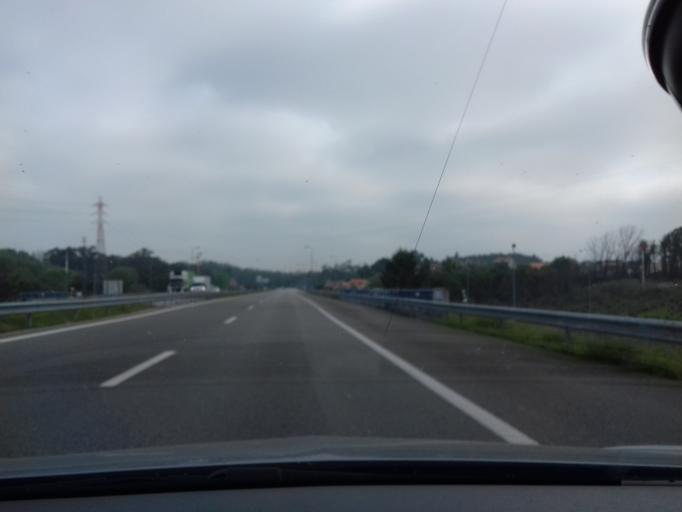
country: PT
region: Aveiro
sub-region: Aveiro
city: Oliveirinha
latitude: 40.5837
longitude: -8.6012
